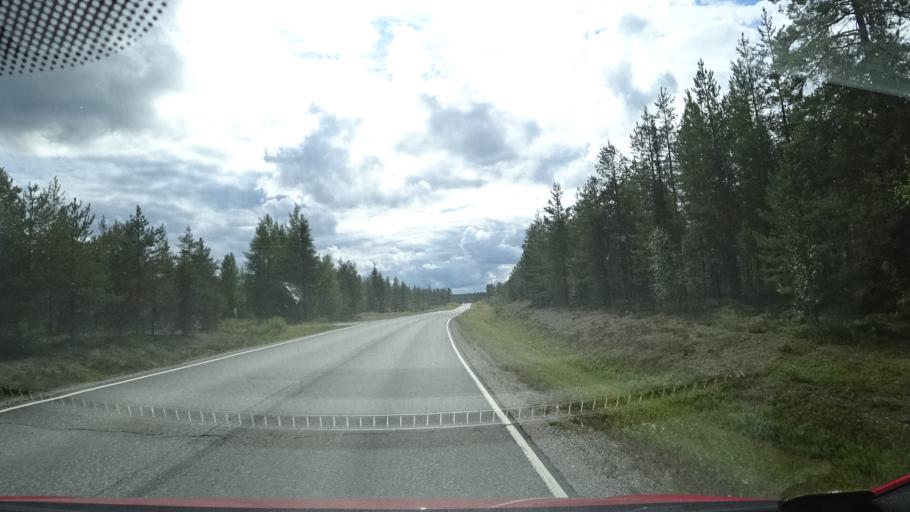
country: FI
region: Lapland
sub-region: Tunturi-Lappi
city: Kittilae
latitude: 67.5026
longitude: 24.8997
